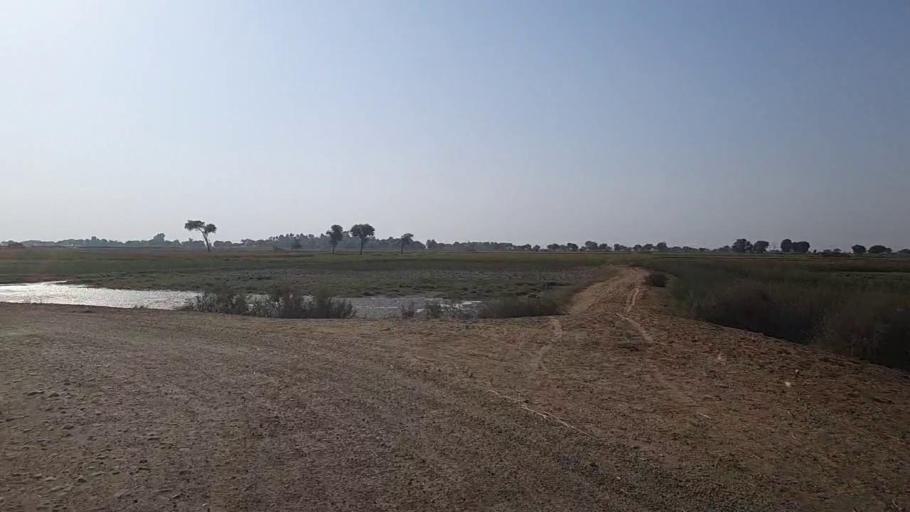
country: PK
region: Sindh
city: Kandhkot
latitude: 28.3762
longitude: 69.3335
